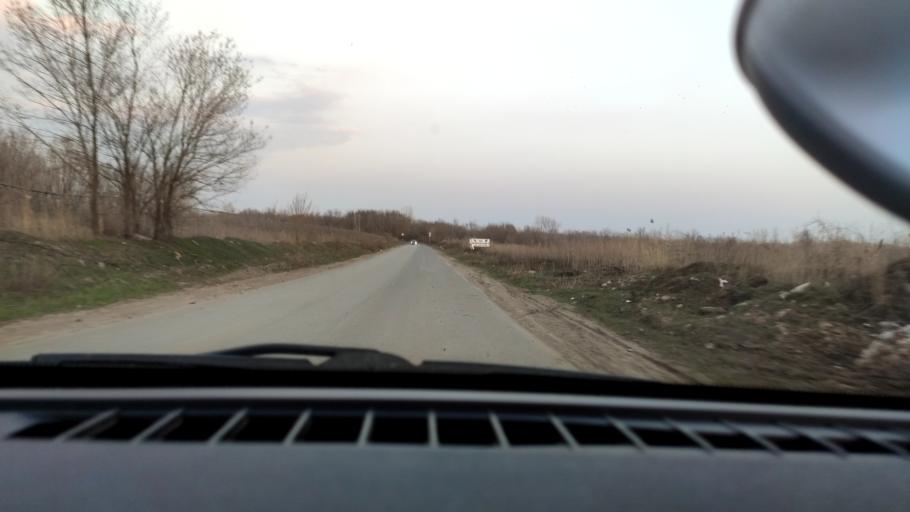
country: RU
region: Samara
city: Smyshlyayevka
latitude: 53.2071
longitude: 50.3113
